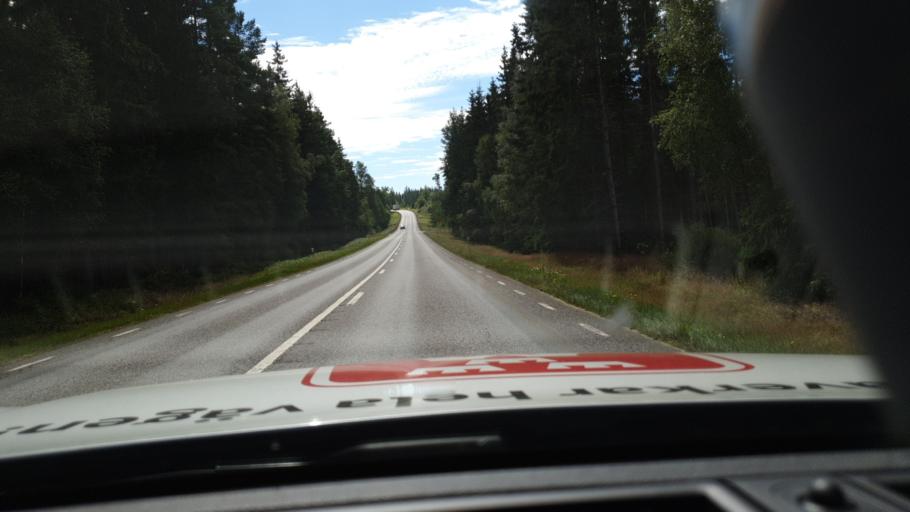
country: SE
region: Kronoberg
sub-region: Vaxjo Kommun
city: Lammhult
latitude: 57.2218
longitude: 14.5096
